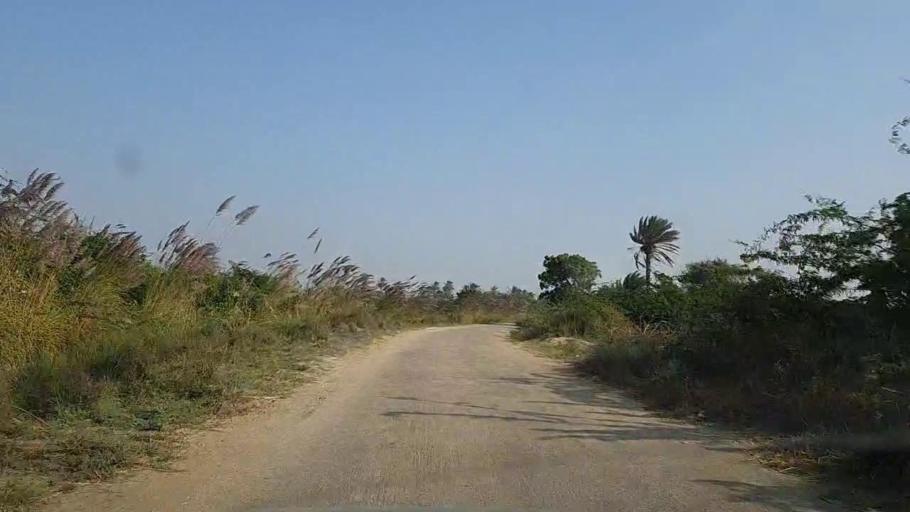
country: PK
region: Sindh
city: Mirpur Sakro
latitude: 24.5943
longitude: 67.6053
